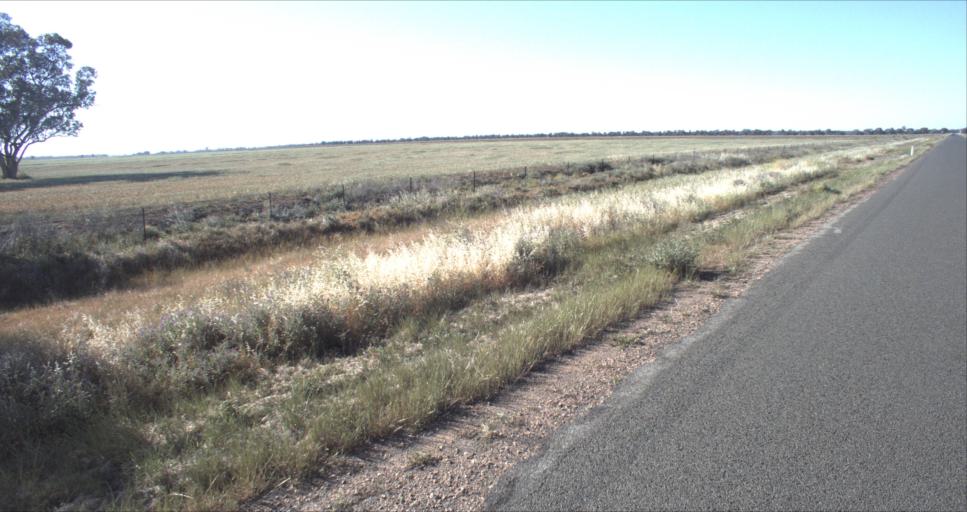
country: AU
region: New South Wales
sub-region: Leeton
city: Leeton
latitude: -34.5641
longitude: 146.2648
